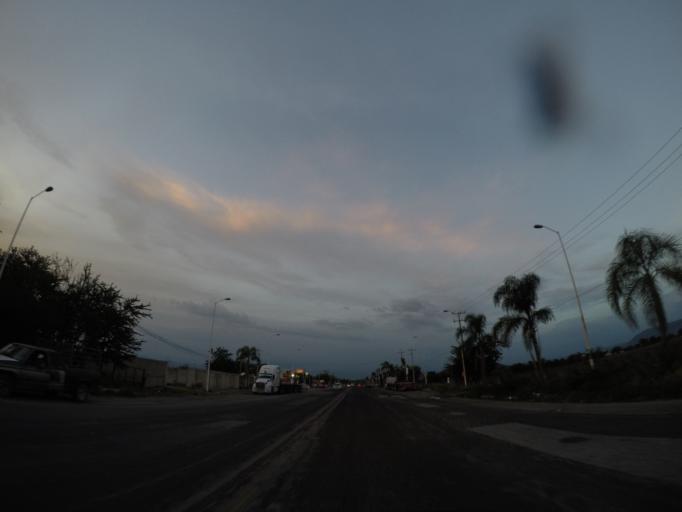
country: MX
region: Morelos
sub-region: Jojutla
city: Tehuixtla
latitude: 18.5931
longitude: -99.2586
